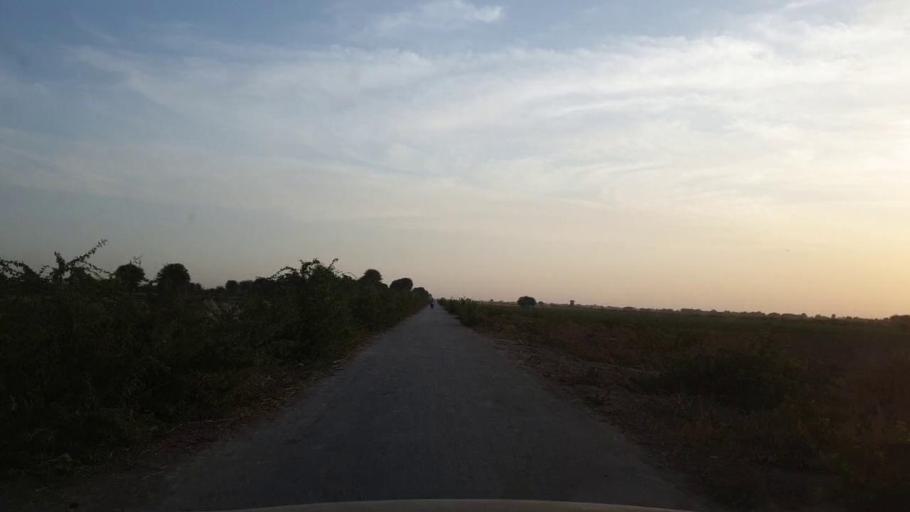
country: PK
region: Sindh
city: Kunri
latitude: 25.1325
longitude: 69.5739
